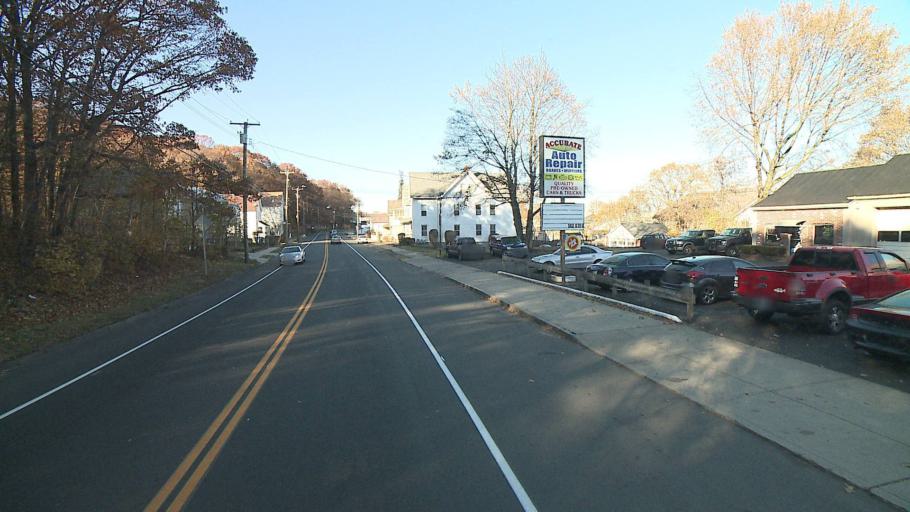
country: US
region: Connecticut
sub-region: New Haven County
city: New Haven
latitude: 41.3247
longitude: -72.8965
